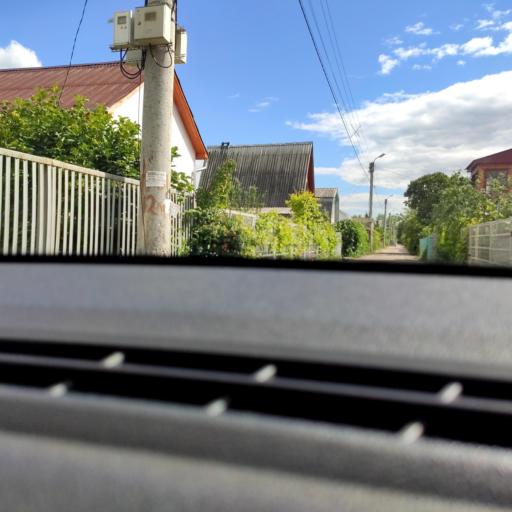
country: RU
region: Samara
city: Podstepki
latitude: 53.5831
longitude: 49.0680
